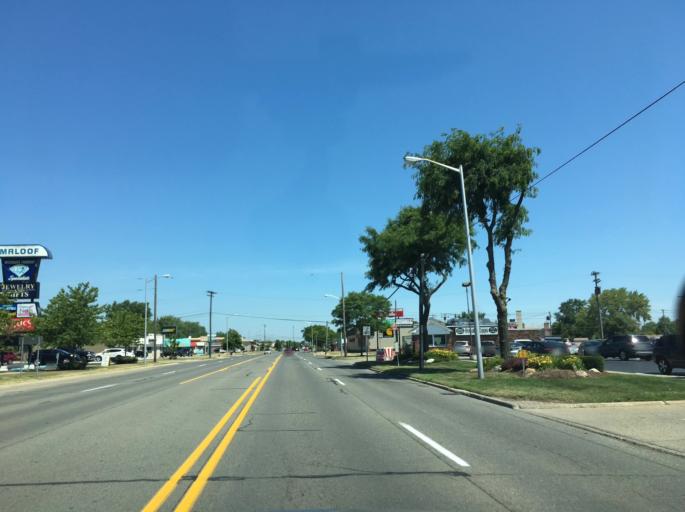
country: US
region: Michigan
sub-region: Macomb County
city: Saint Clair Shores
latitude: 42.5036
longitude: -82.8979
